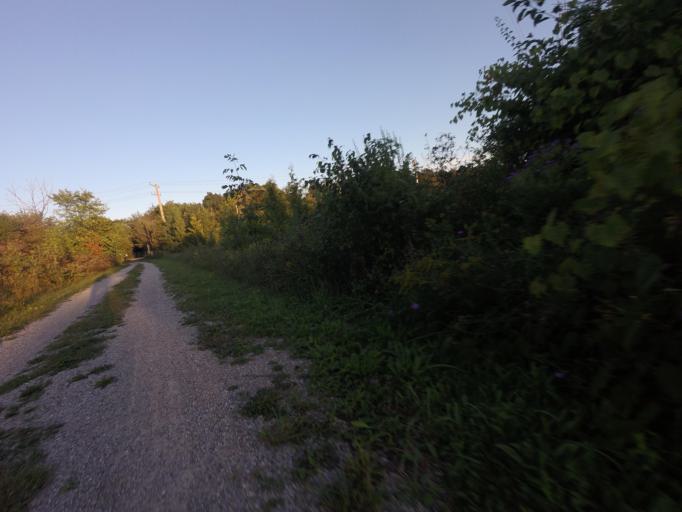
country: CA
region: Ontario
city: Goderich
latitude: 43.7497
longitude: -81.6551
